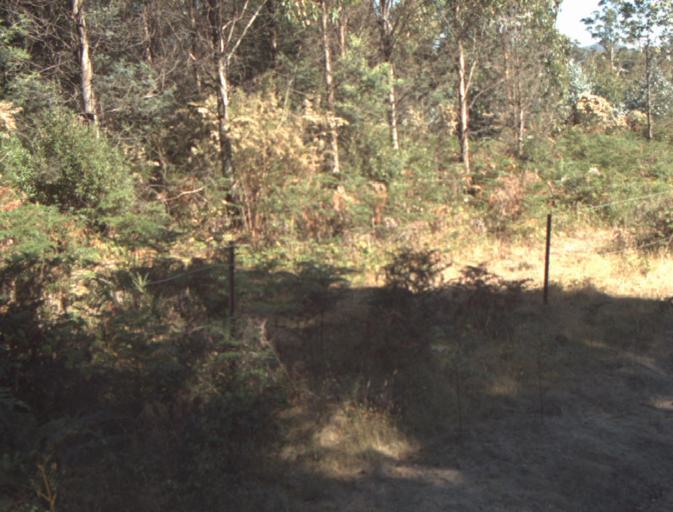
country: AU
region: Tasmania
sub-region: Dorset
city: Scottsdale
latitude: -41.2692
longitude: 147.3762
